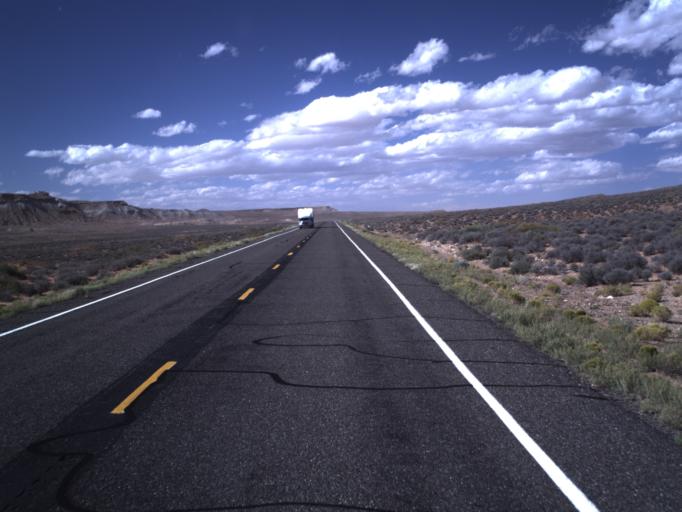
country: US
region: Utah
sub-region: Wayne County
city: Loa
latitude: 38.0827
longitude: -110.6135
